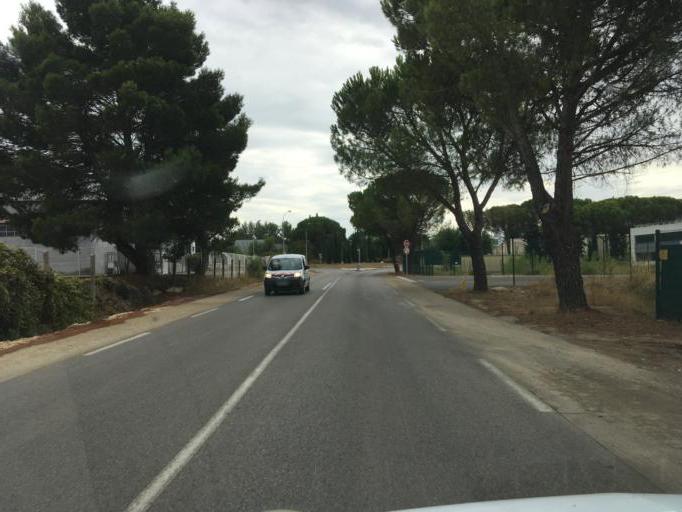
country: FR
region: Provence-Alpes-Cote d'Azur
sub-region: Departement des Bouches-du-Rhone
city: Rousset
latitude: 43.4691
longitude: 5.6140
